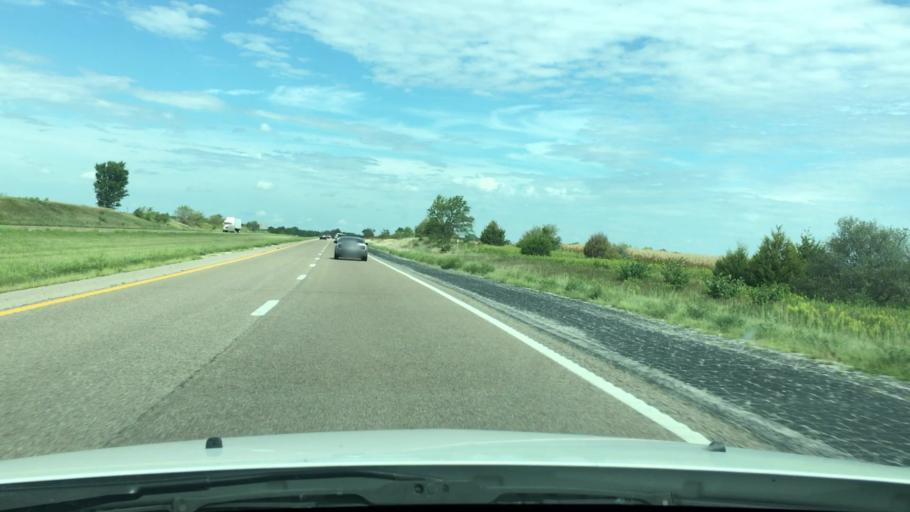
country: US
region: Missouri
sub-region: Audrain County
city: Mexico
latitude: 39.0309
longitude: -91.8865
